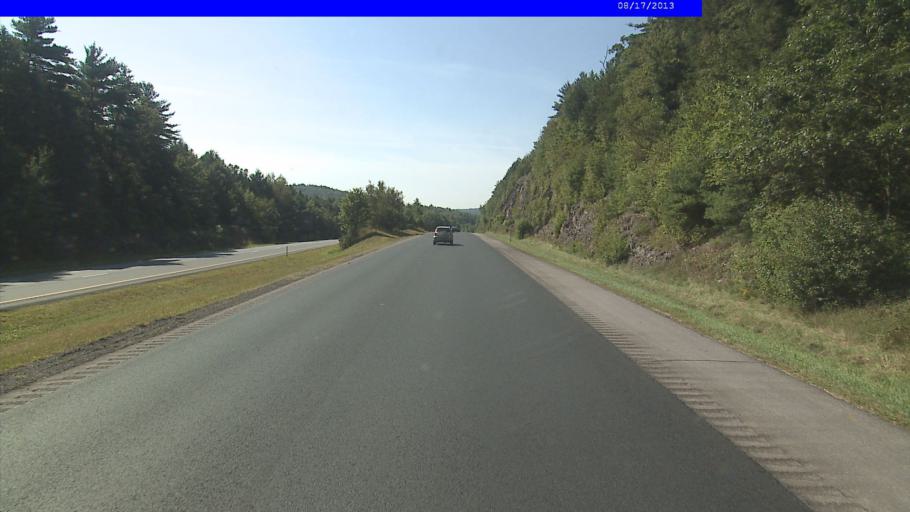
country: US
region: Vermont
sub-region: Windham County
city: Bellows Falls
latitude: 43.1490
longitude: -72.4750
